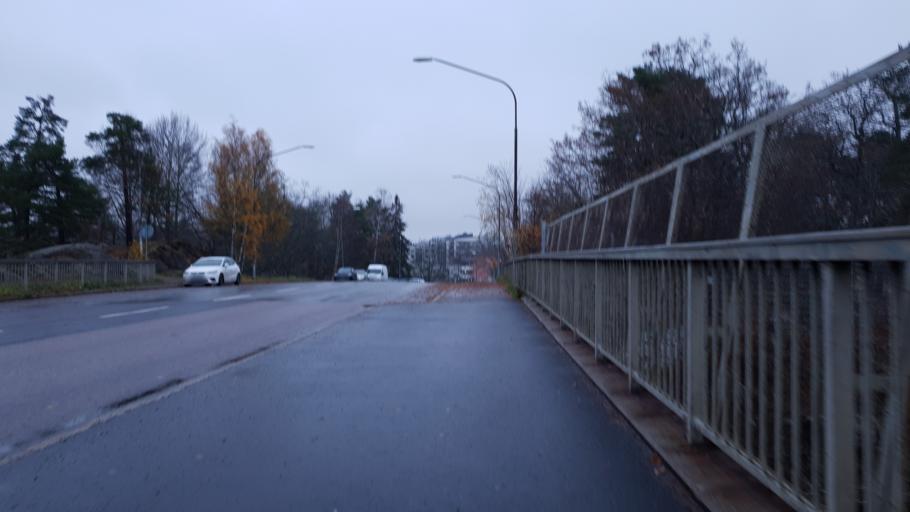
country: SE
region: Stockholm
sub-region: Stockholms Kommun
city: Arsta
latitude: 59.2425
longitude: 18.0797
